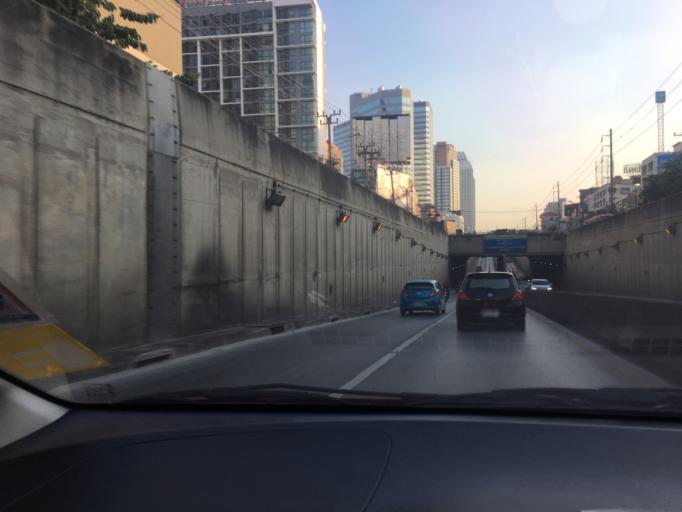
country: TH
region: Bangkok
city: Huai Khwang
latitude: 13.7797
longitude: 100.5737
